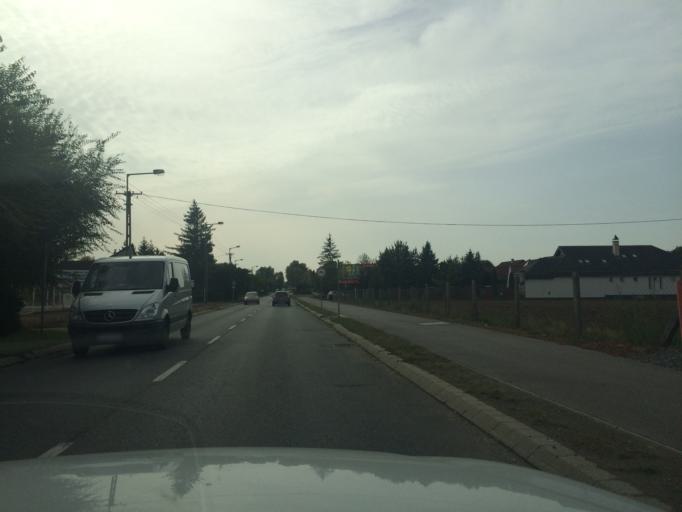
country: HU
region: Szabolcs-Szatmar-Bereg
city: Nyiregyhaza
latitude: 47.9870
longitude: 21.7291
